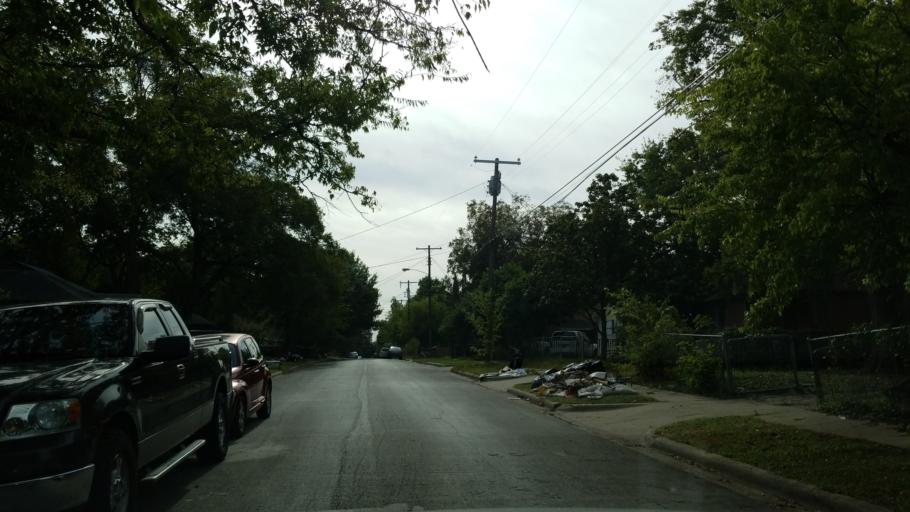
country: US
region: Texas
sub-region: Dallas County
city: Dallas
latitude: 32.7848
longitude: -96.7204
